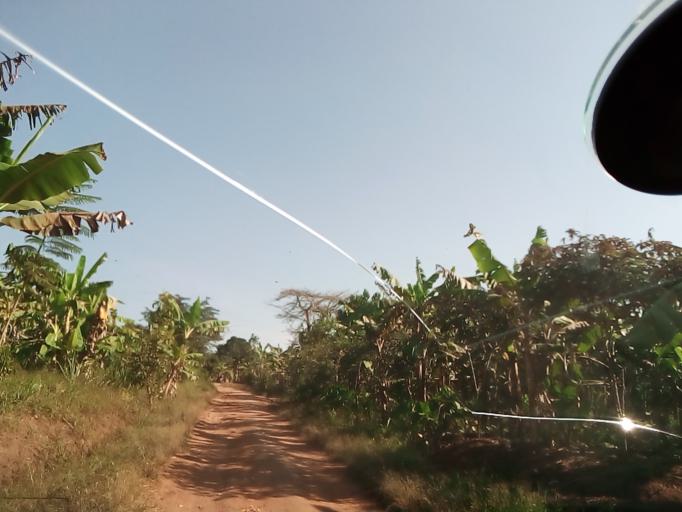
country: UG
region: Central Region
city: Masaka
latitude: -0.2664
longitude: 31.7220
